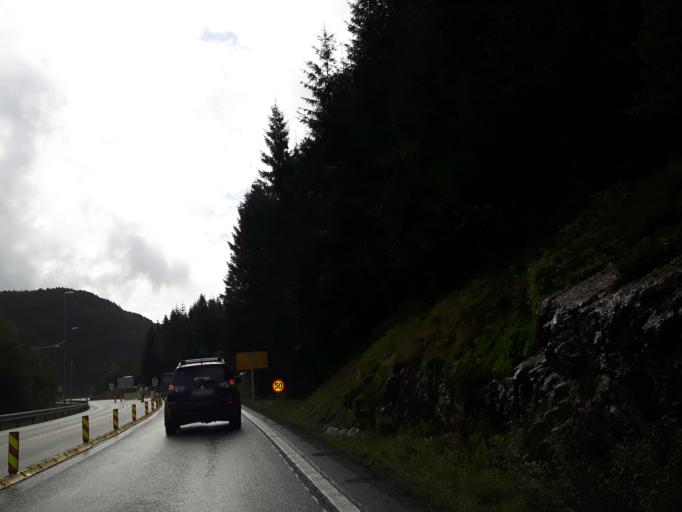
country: NO
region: Rogaland
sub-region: Lund
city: Moi
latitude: 58.4000
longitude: 6.6275
